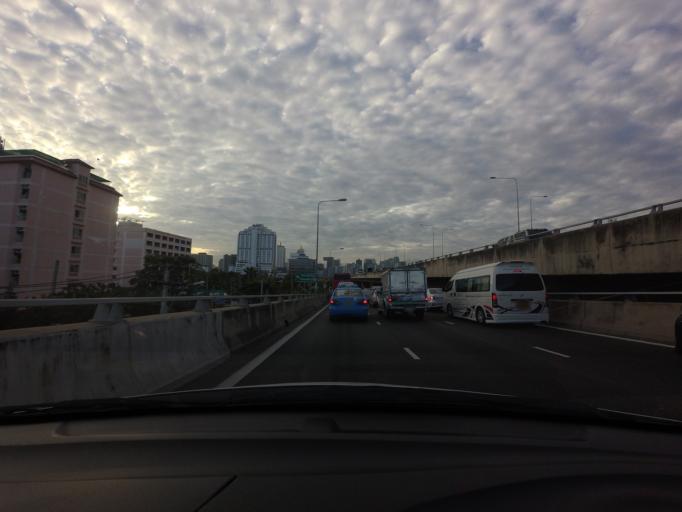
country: TH
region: Bangkok
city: Huai Khwang
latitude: 13.7538
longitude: 100.5851
